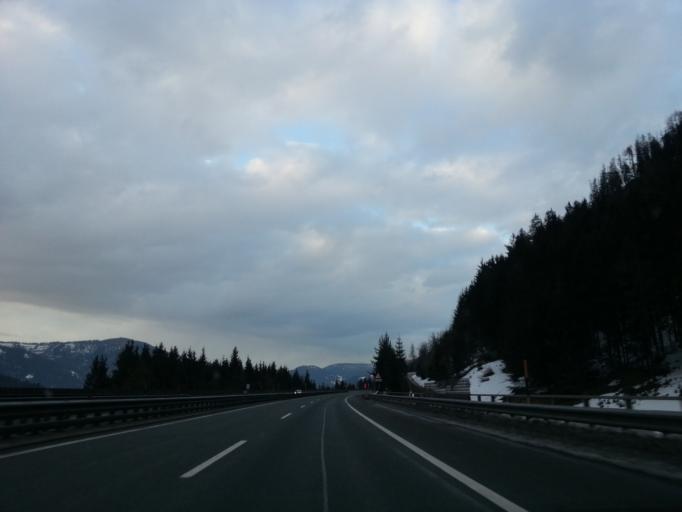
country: AT
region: Salzburg
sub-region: Politischer Bezirk Sankt Johann im Pongau
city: Flachau
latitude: 47.3333
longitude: 13.3940
